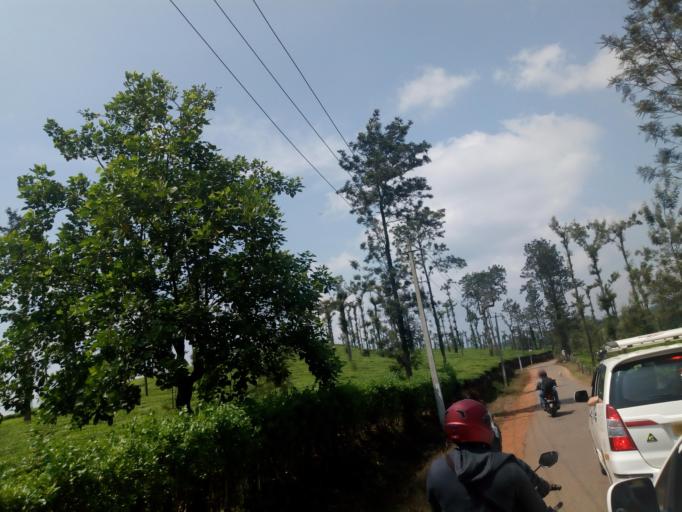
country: IN
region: Karnataka
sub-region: Kodagu
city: Ponnampet
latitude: 12.0304
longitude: 75.9448
